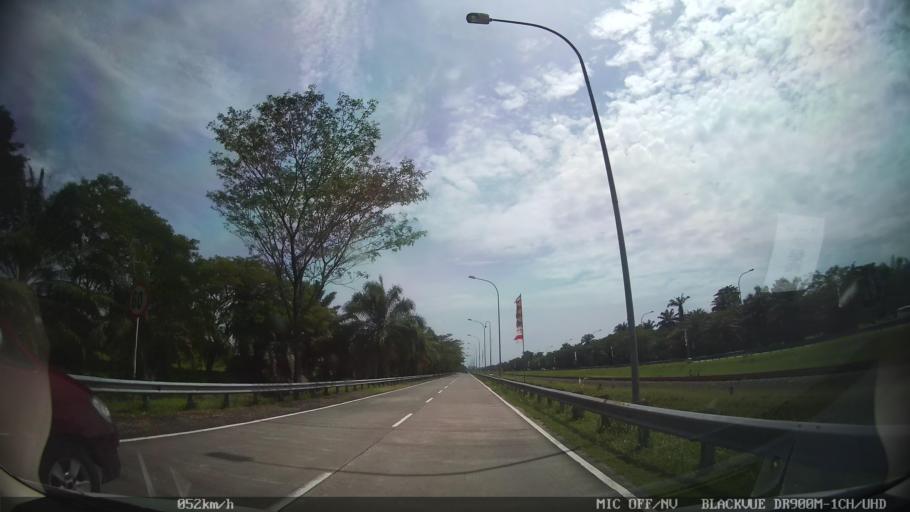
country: ID
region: North Sumatra
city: Percut
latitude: 3.6200
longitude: 98.8633
